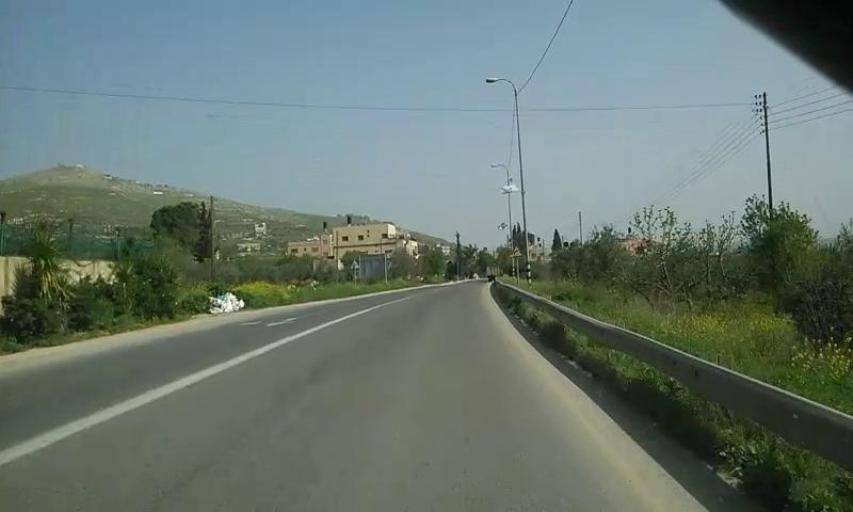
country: PS
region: West Bank
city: Huwwarah
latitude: 32.1645
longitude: 35.2627
